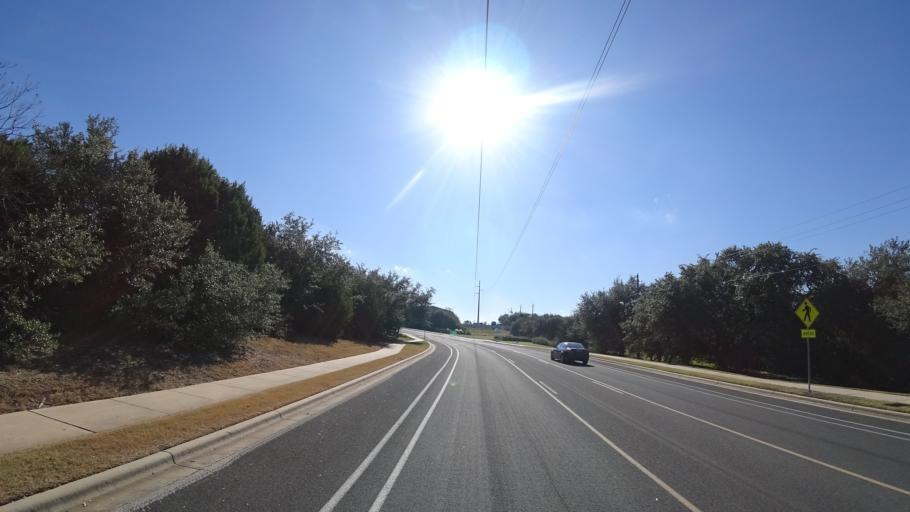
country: US
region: Texas
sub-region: Travis County
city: Hudson Bend
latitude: 30.3715
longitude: -97.8956
